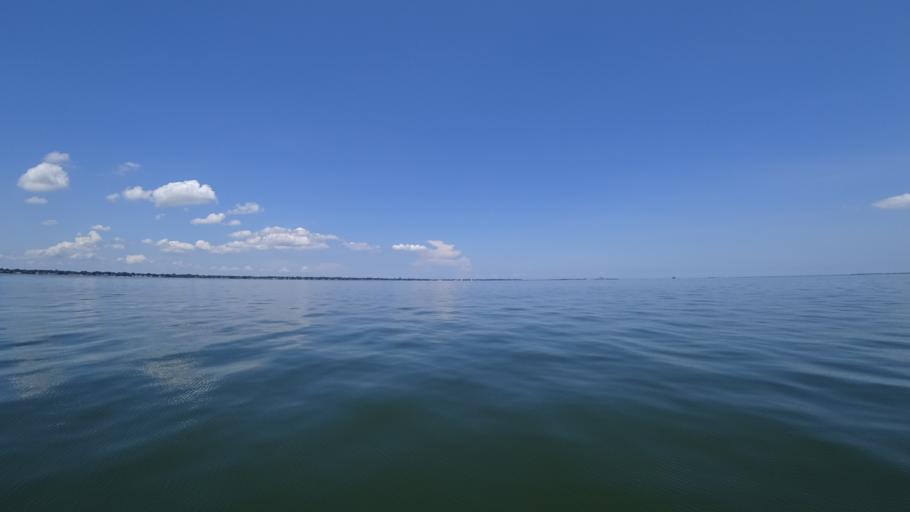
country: US
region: Virginia
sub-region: City of Newport News
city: Newport News
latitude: 36.9674
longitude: -76.3760
